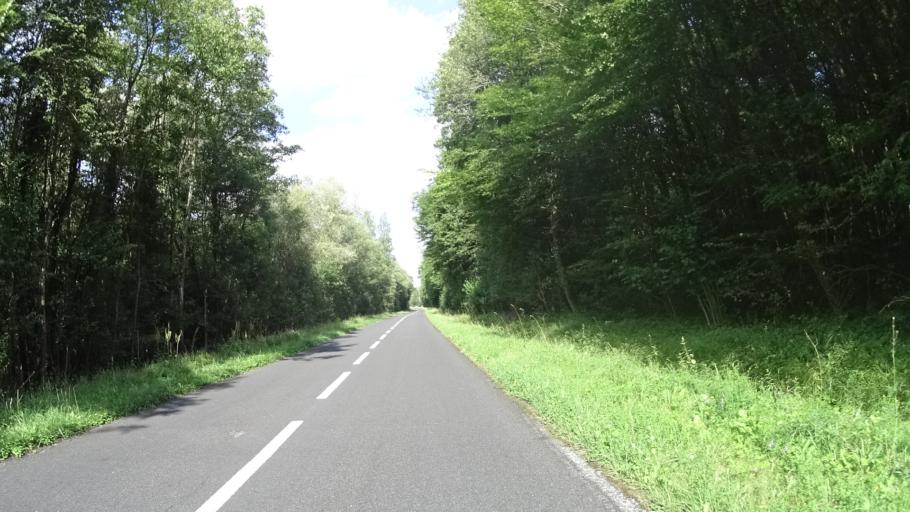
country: FR
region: Lorraine
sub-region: Departement de Meurthe-et-Moselle
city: Gondreville
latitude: 48.6473
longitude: 5.9687
